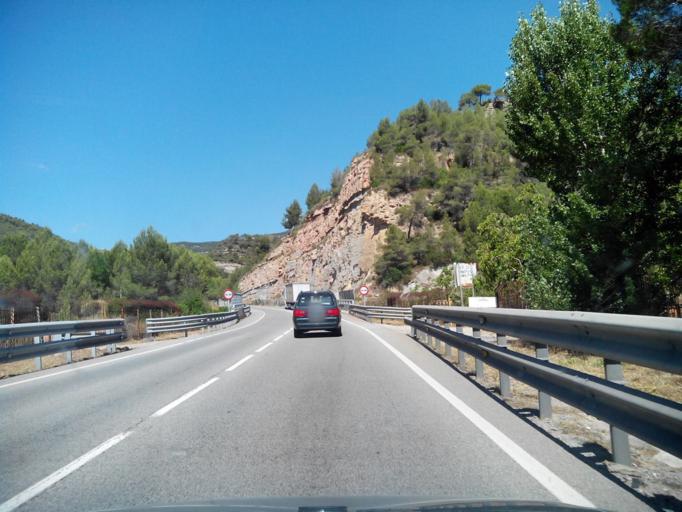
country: ES
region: Catalonia
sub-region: Provincia de Barcelona
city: Monistrol de Montserrat
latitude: 41.6236
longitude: 1.8537
